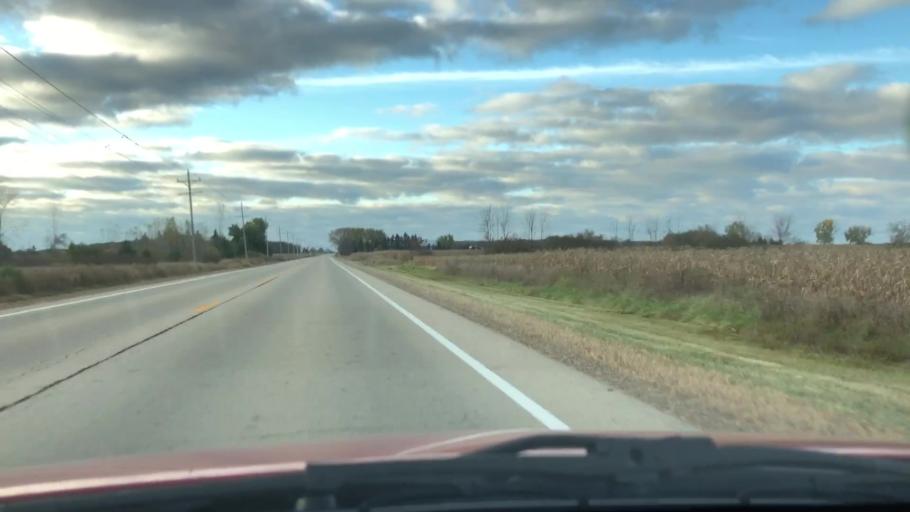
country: US
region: Wisconsin
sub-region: Outagamie County
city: Seymour
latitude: 44.4779
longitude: -88.2911
